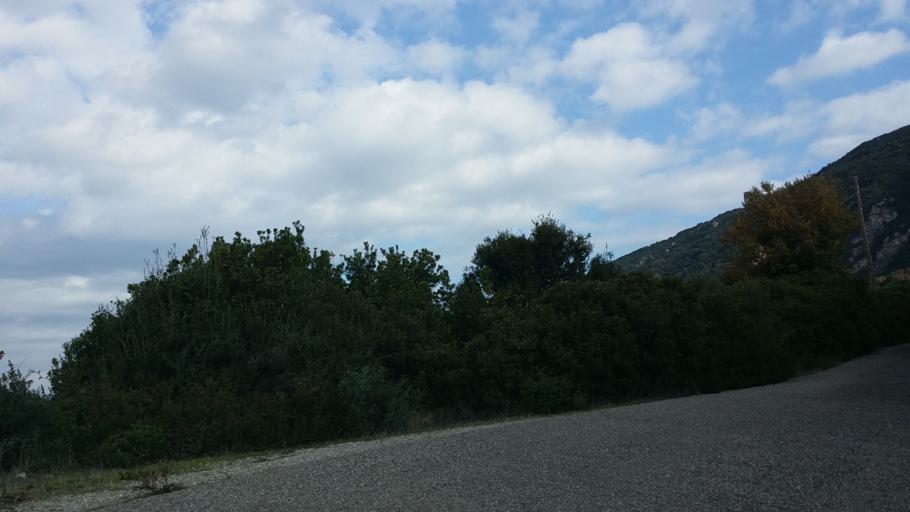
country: GR
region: West Greece
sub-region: Nomos Aitolias kai Akarnanias
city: Katouna
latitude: 38.8492
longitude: 21.0519
